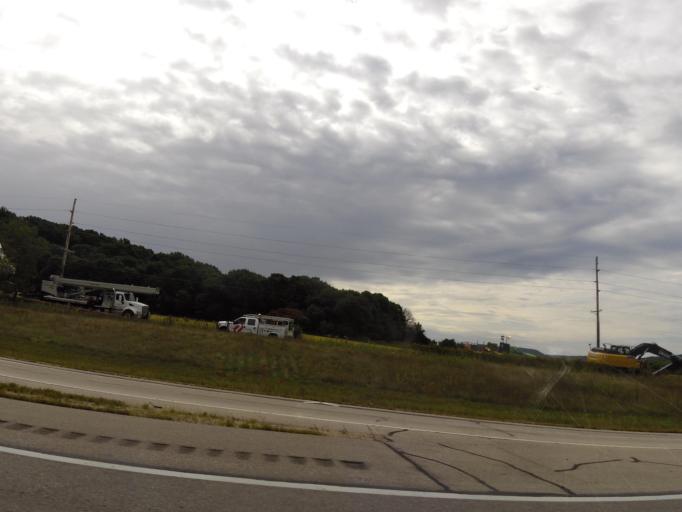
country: US
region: Wisconsin
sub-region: La Crosse County
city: Bangor
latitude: 43.8996
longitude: -90.9172
